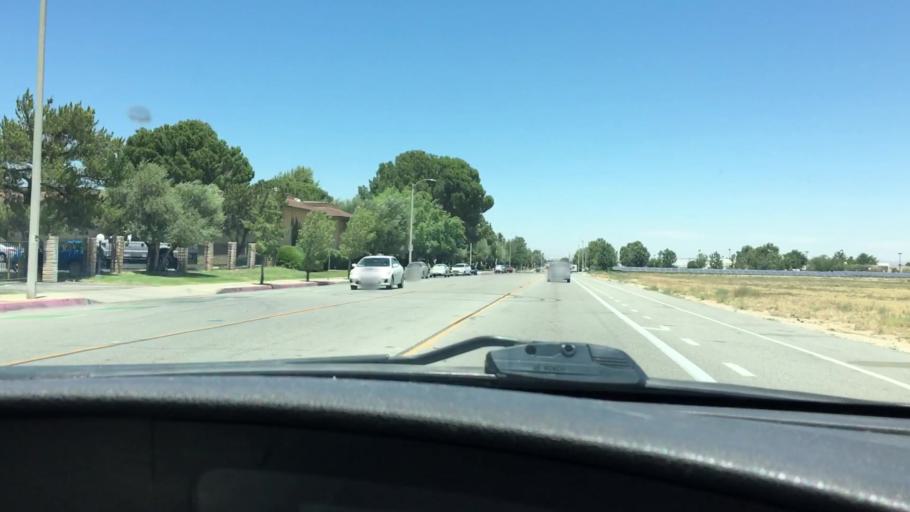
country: US
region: California
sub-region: Los Angeles County
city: Lancaster
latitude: 34.6610
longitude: -118.1567
